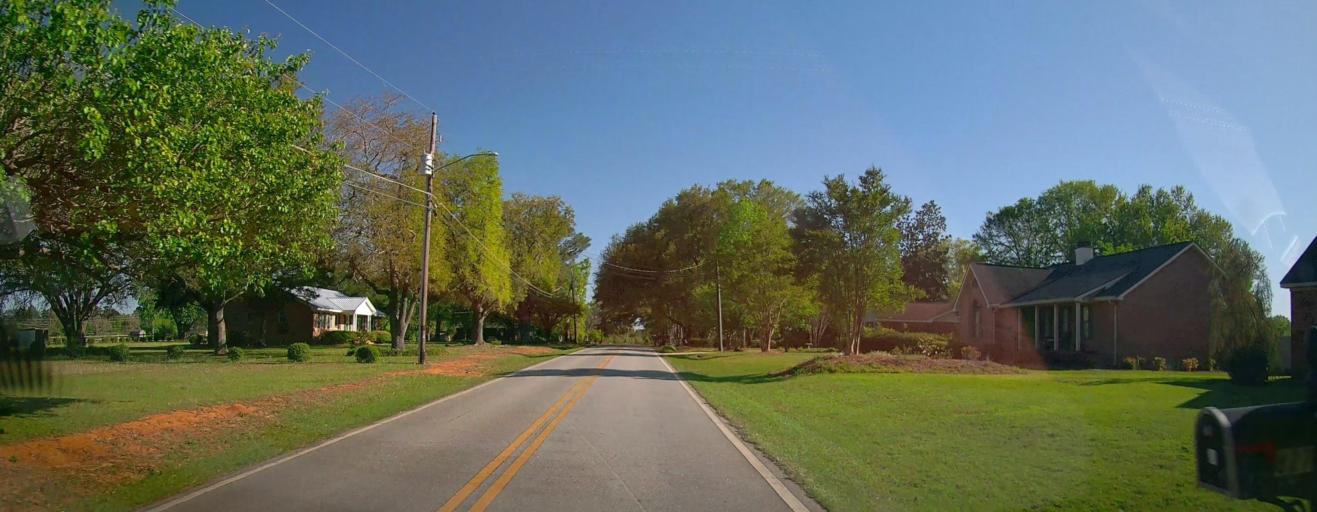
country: US
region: Georgia
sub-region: Houston County
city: Perry
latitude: 32.4530
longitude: -83.7080
